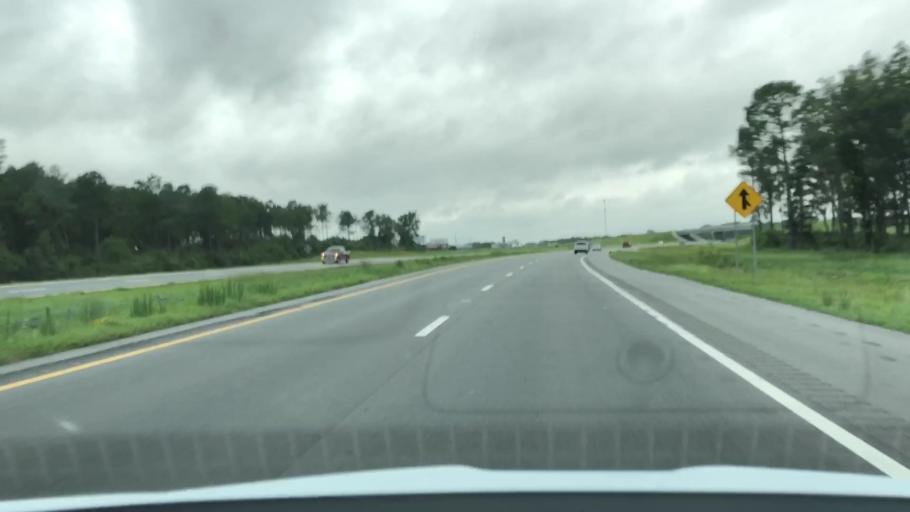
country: US
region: North Carolina
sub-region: Lenoir County
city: La Grange
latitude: 35.3006
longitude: -77.8148
